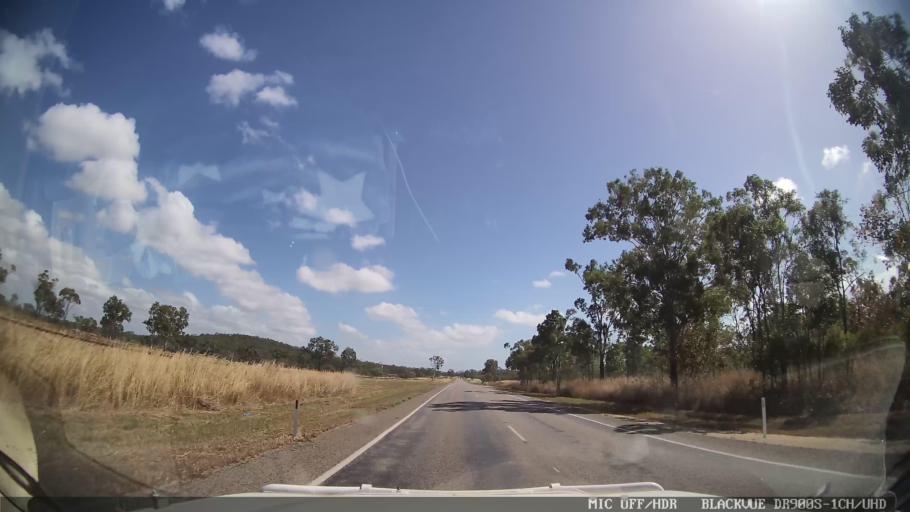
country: AU
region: Queensland
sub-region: Whitsunday
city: Red Hill
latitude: -20.1843
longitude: 148.3544
